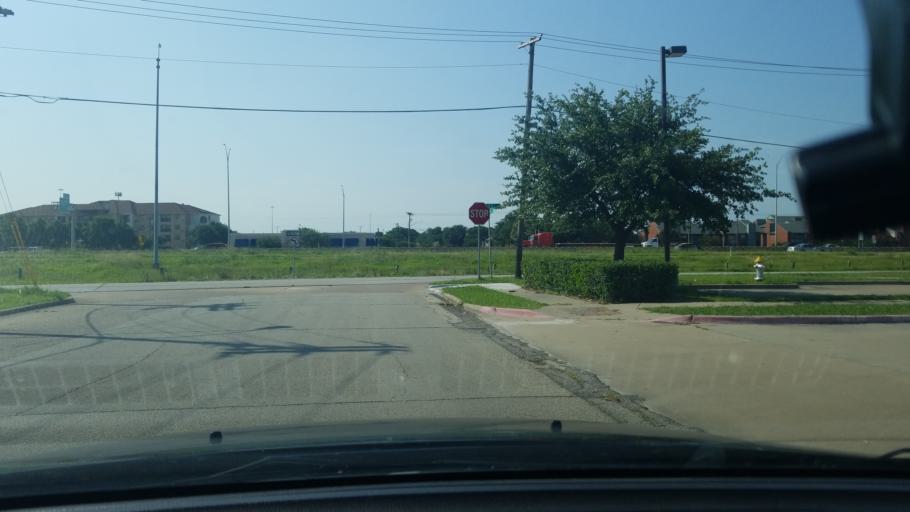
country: US
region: Texas
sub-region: Dallas County
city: Mesquite
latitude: 32.8217
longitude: -96.6341
